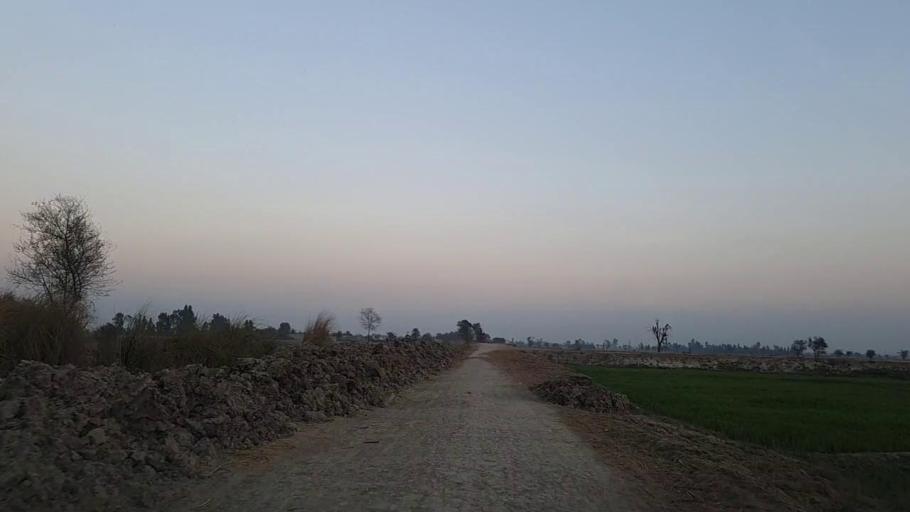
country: PK
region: Sindh
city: Naushahro Firoz
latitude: 26.7942
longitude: 68.0390
